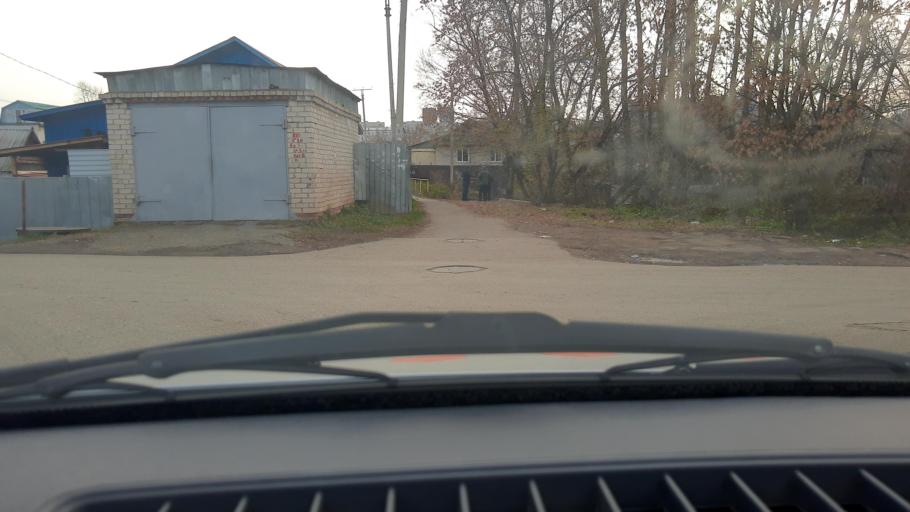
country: RU
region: Bashkortostan
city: Ufa
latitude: 54.7409
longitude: 55.9102
